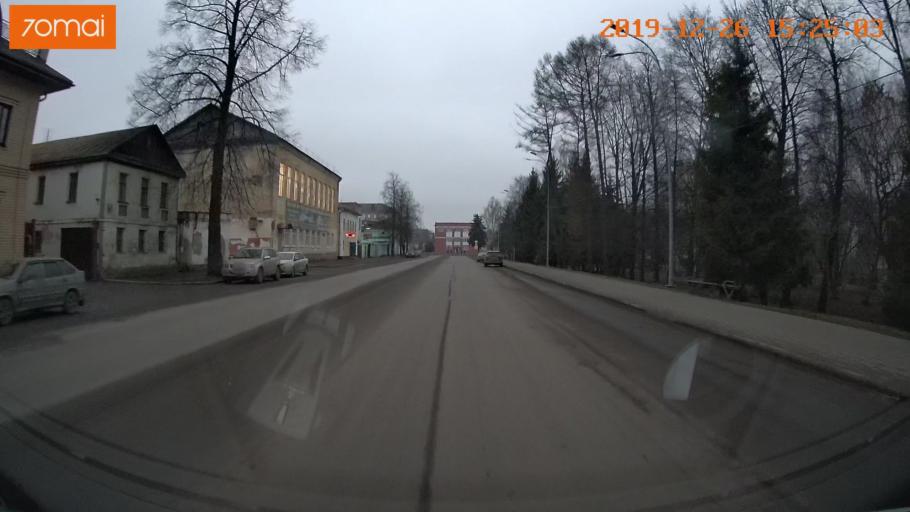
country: RU
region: Jaroslavl
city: Rybinsk
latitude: 58.0522
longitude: 38.8415
